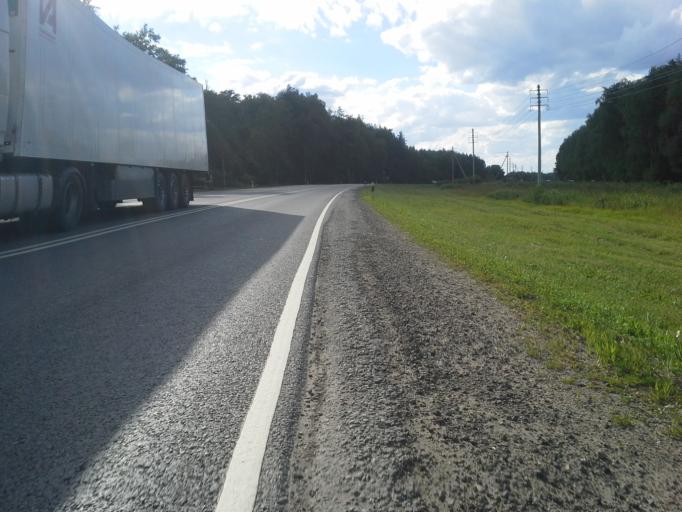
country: RU
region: Moskovskaya
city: L'vovskiy
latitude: 55.3351
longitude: 37.4733
